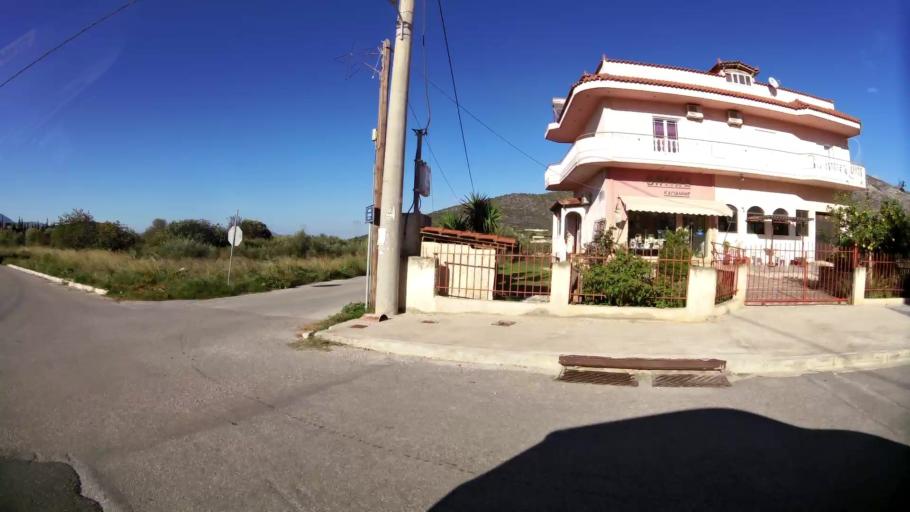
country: GR
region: Attica
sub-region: Nomarchia Anatolikis Attikis
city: Kalyvia Thorikou
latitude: 37.8423
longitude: 23.9318
